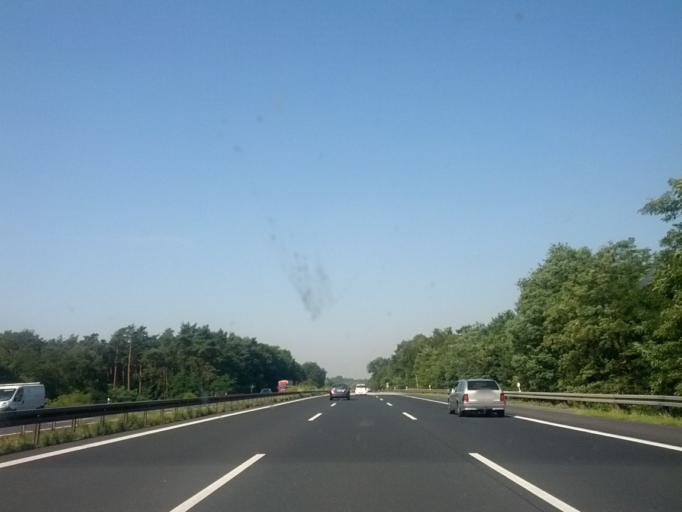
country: DE
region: Brandenburg
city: Rangsdorf
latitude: 52.3070
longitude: 13.3866
